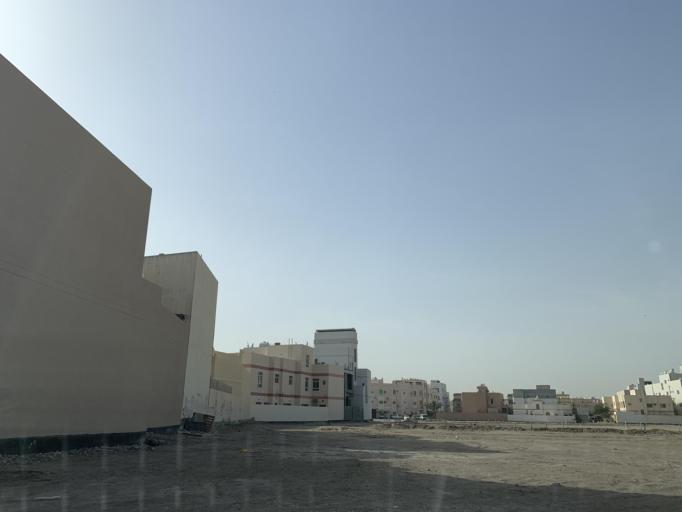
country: BH
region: Northern
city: Madinat `Isa
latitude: 26.1822
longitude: 50.5627
